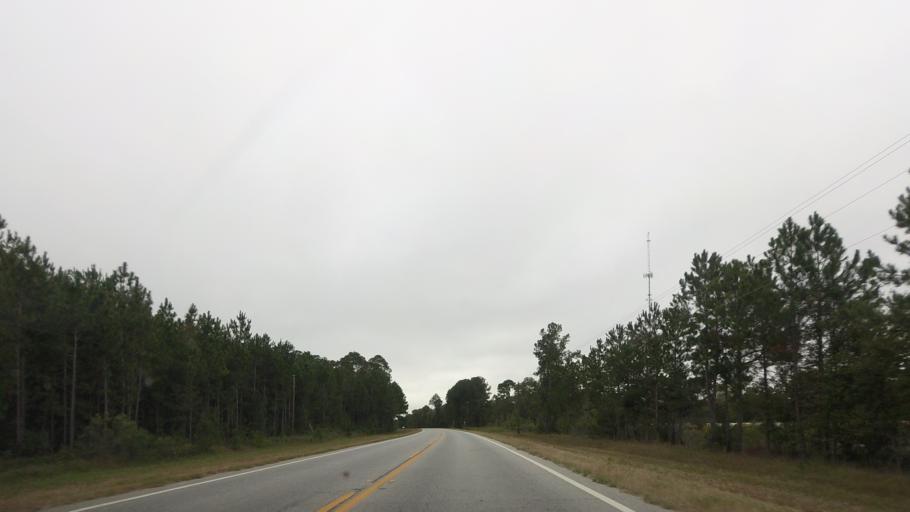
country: US
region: Georgia
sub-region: Berrien County
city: Ray City
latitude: 31.1424
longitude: -83.2174
